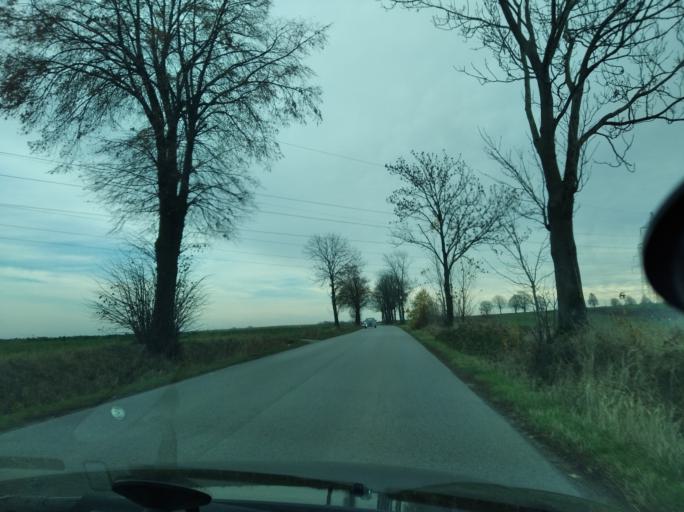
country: PL
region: Subcarpathian Voivodeship
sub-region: Powiat lancucki
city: Wysoka
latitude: 50.0248
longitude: 22.2554
